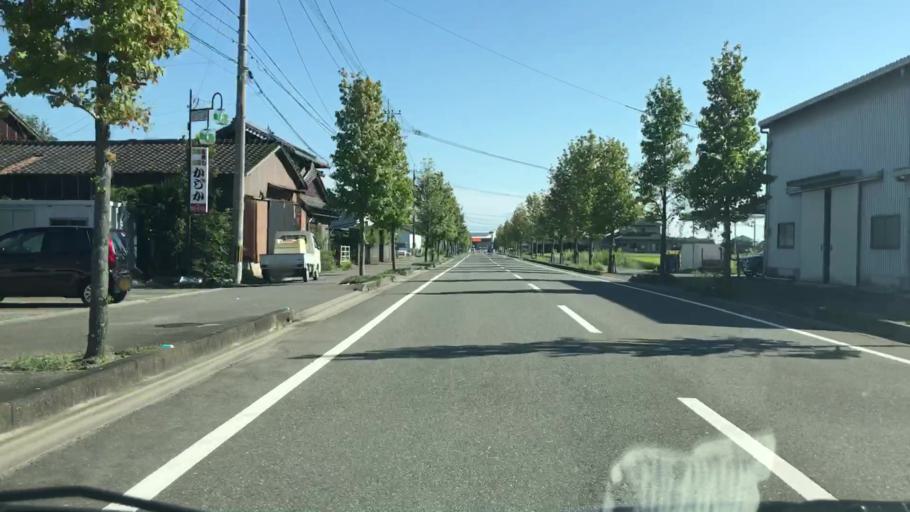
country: JP
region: Saga Prefecture
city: Okawa
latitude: 33.1846
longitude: 130.3138
